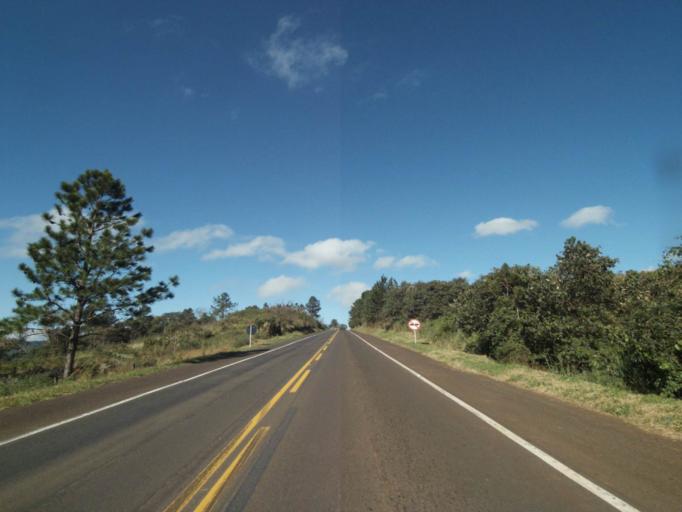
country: BR
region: Parana
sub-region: Faxinal
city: Faxinal
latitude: -23.8623
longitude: -51.1677
